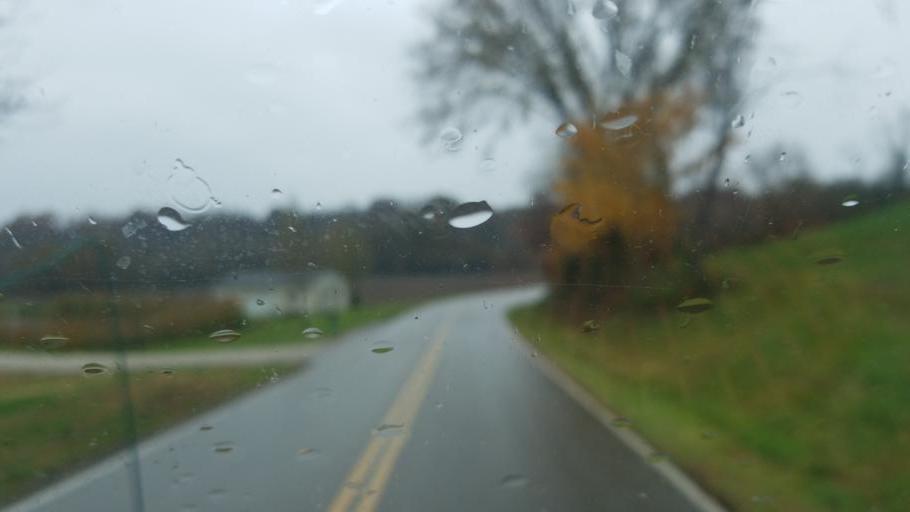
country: US
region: West Virginia
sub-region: Wood County
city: Blennerhassett
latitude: 39.3326
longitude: -81.6220
